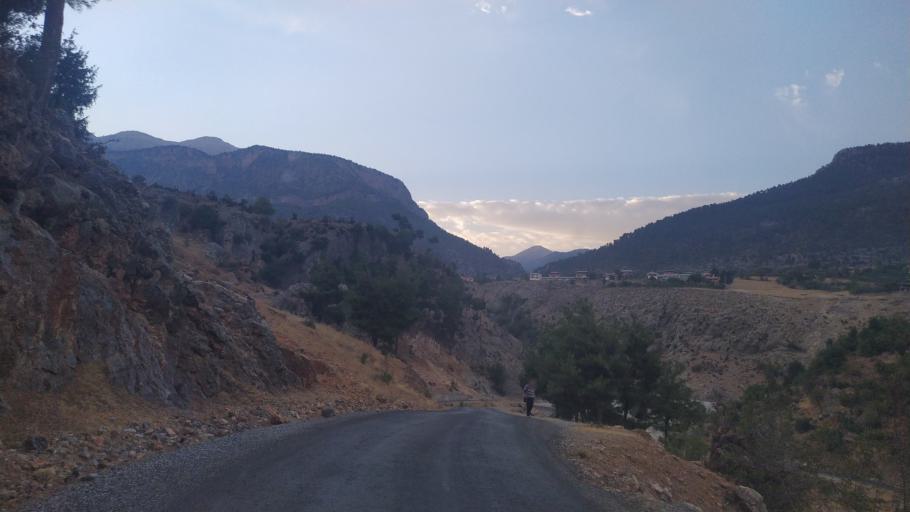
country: TR
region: Mersin
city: Camliyayla
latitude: 37.2384
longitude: 34.7140
